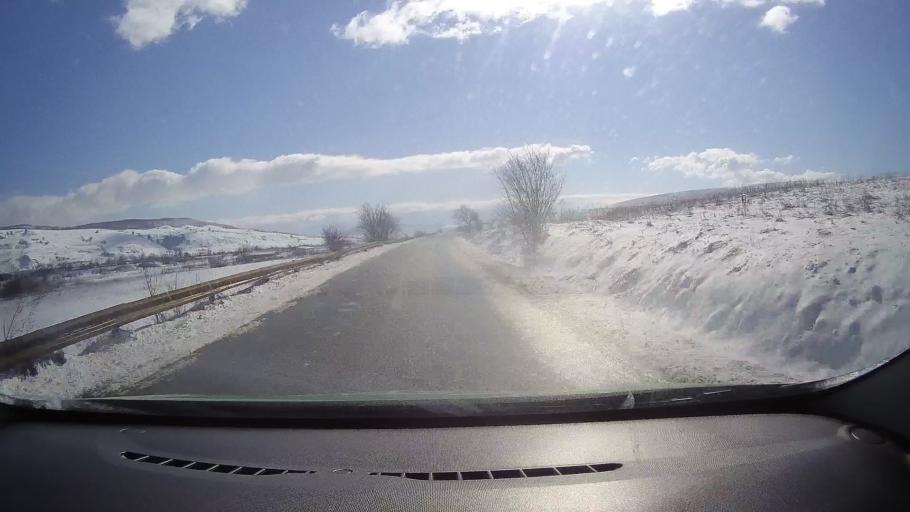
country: RO
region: Sibiu
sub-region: Comuna Rosia
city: Rosia
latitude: 45.8340
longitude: 24.3103
